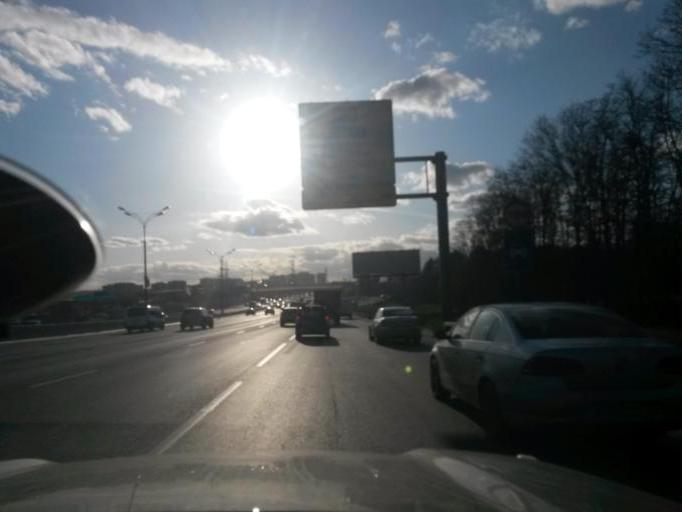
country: RU
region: Moscow
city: Annino
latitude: 55.5756
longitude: 37.6066
